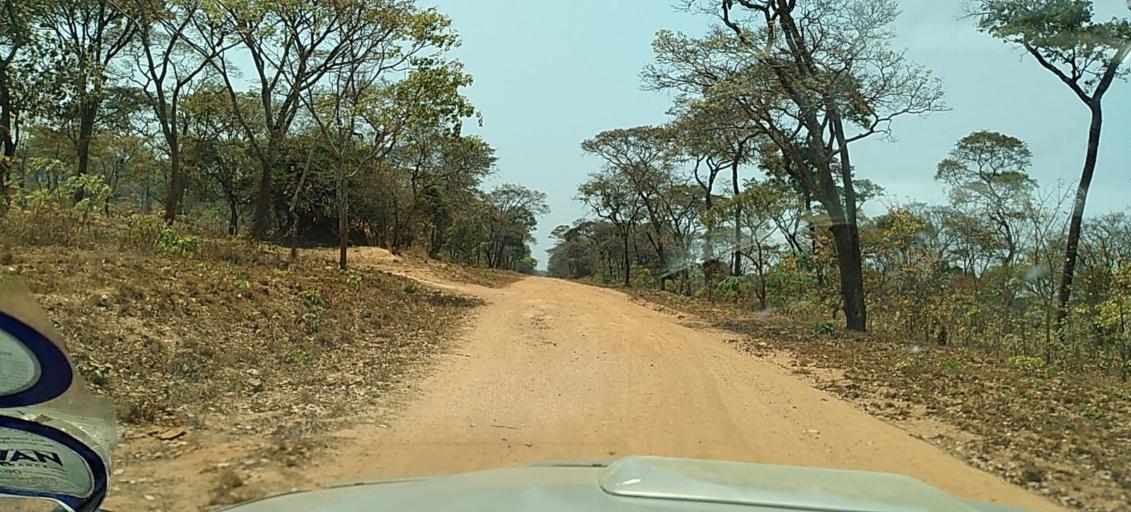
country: ZM
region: North-Western
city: Kasempa
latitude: -13.5483
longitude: 26.0327
